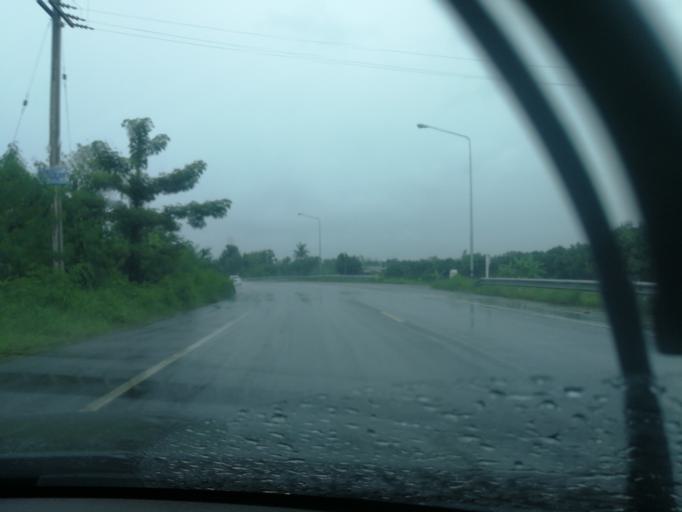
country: TH
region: Chiang Mai
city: San Pa Tong
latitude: 18.6347
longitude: 98.8587
